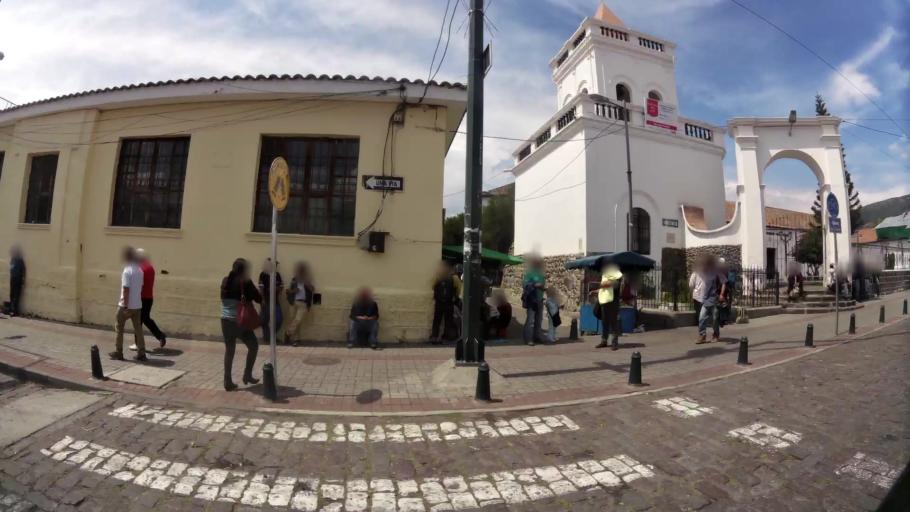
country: EC
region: Pichincha
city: Quito
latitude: -0.2128
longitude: -78.4044
